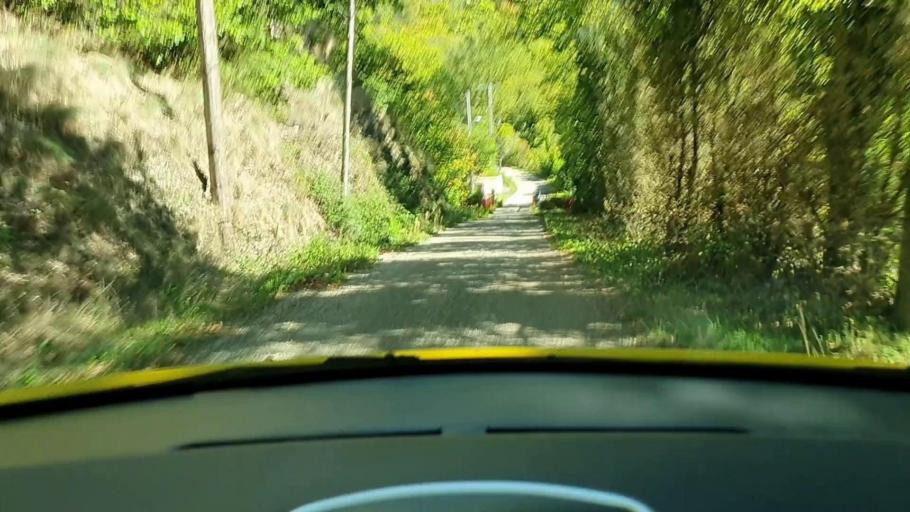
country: FR
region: Languedoc-Roussillon
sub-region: Departement du Gard
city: Le Vigan
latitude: 43.9937
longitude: 3.4613
